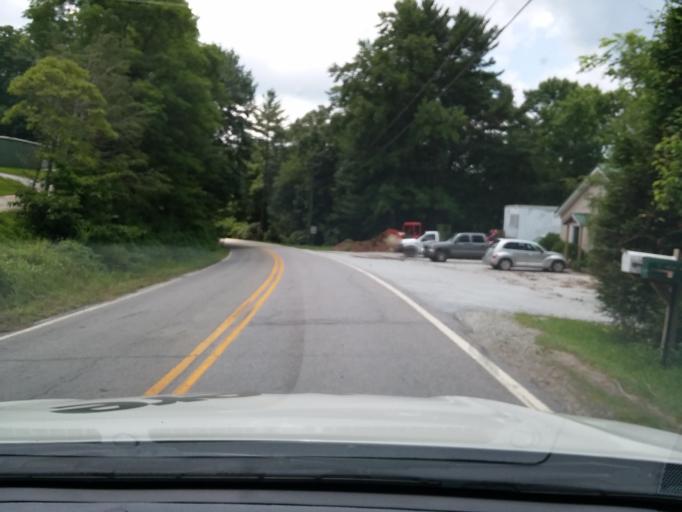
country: US
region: Georgia
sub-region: Rabun County
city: Mountain City
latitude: 35.0402
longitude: -83.2023
